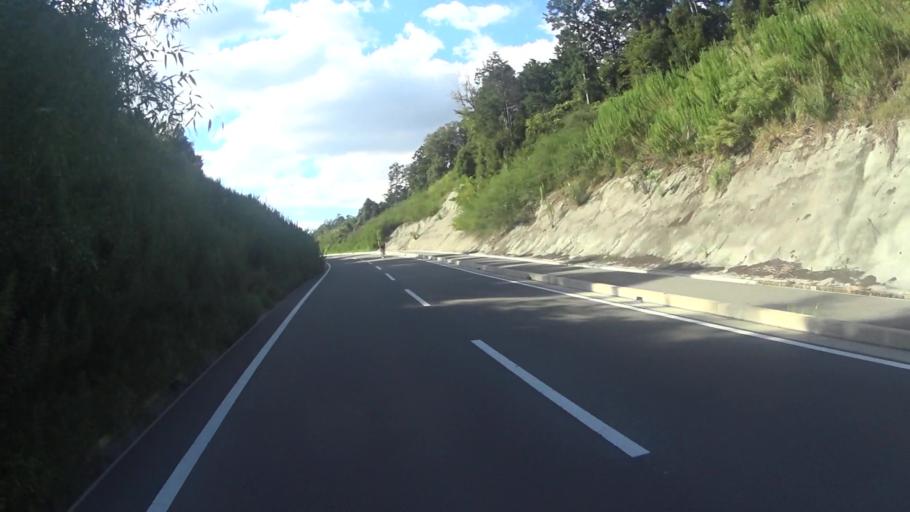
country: JP
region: Kyoto
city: Uji
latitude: 34.8408
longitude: 135.8493
